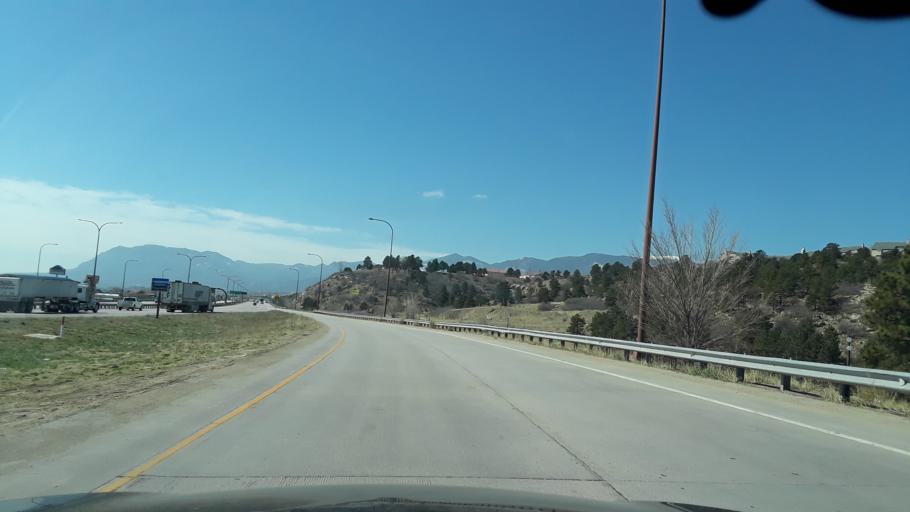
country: US
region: Colorado
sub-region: El Paso County
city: Colorado Springs
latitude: 38.9096
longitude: -104.8252
